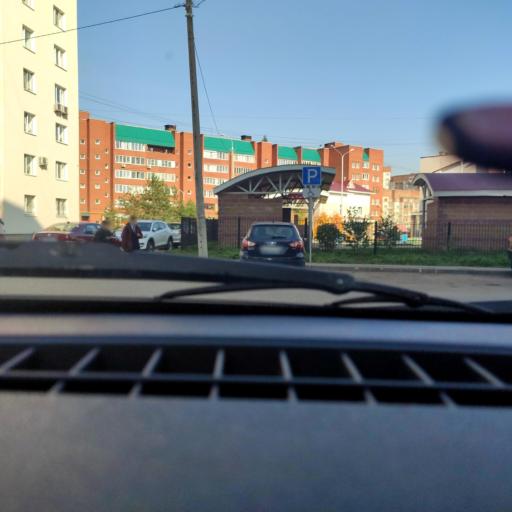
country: RU
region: Bashkortostan
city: Ufa
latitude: 54.7622
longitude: 56.0524
